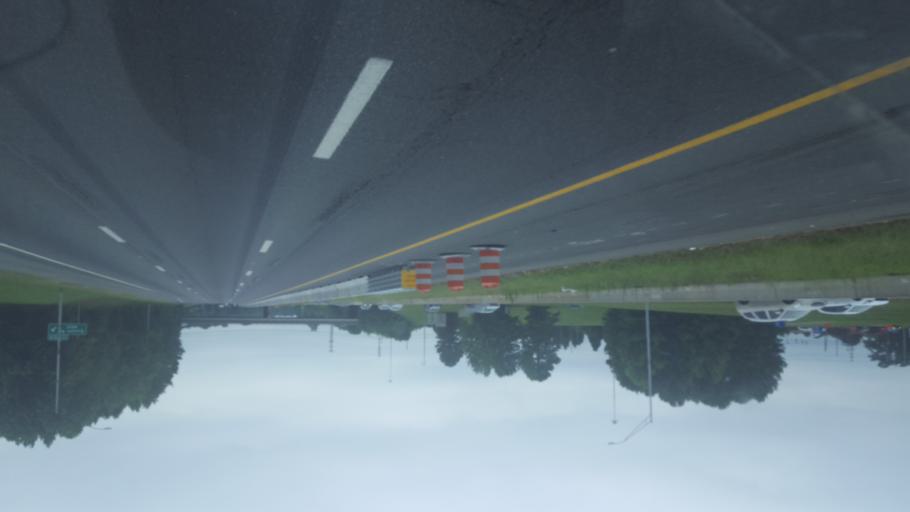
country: US
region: North Carolina
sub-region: Mecklenburg County
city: Charlotte
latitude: 35.3049
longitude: -80.8486
